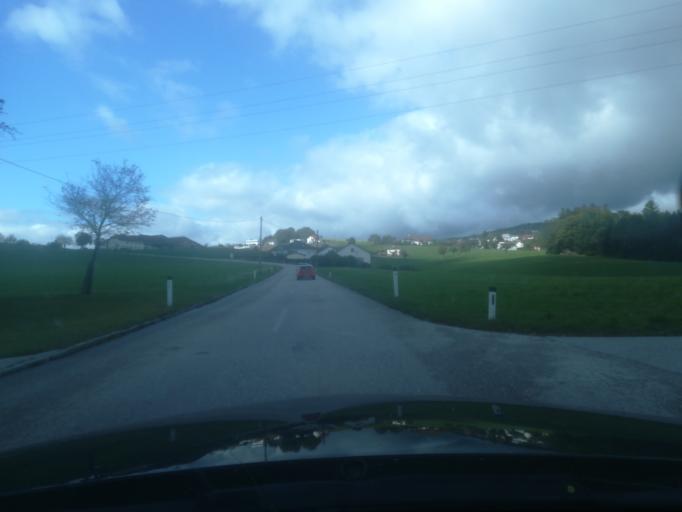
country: AT
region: Upper Austria
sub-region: Linz Stadt
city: Linz
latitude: 48.3510
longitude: 14.2641
